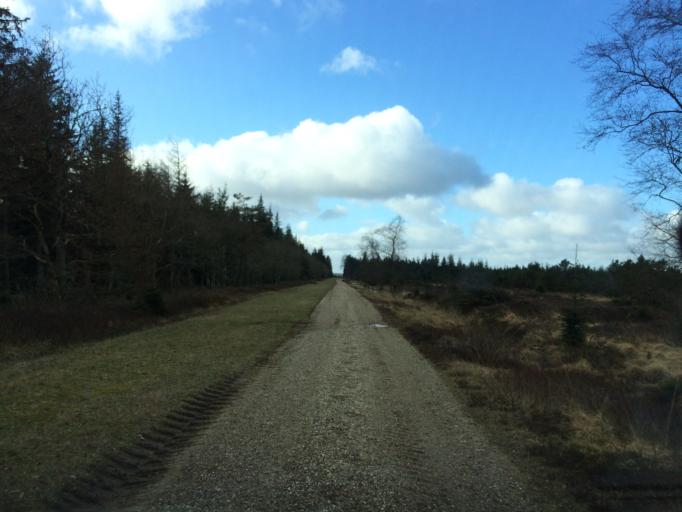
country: DK
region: Central Jutland
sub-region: Holstebro Kommune
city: Ulfborg
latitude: 56.2559
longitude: 8.4468
